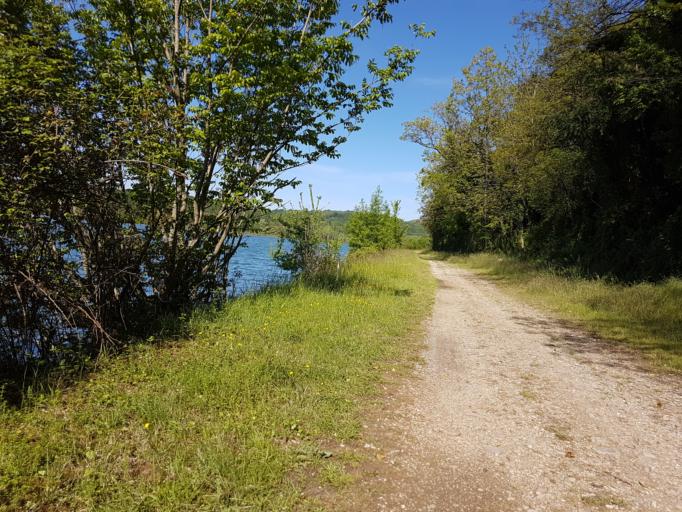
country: FR
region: Rhone-Alpes
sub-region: Departement de l'Ain
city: Villebois
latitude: 45.8378
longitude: 5.4282
